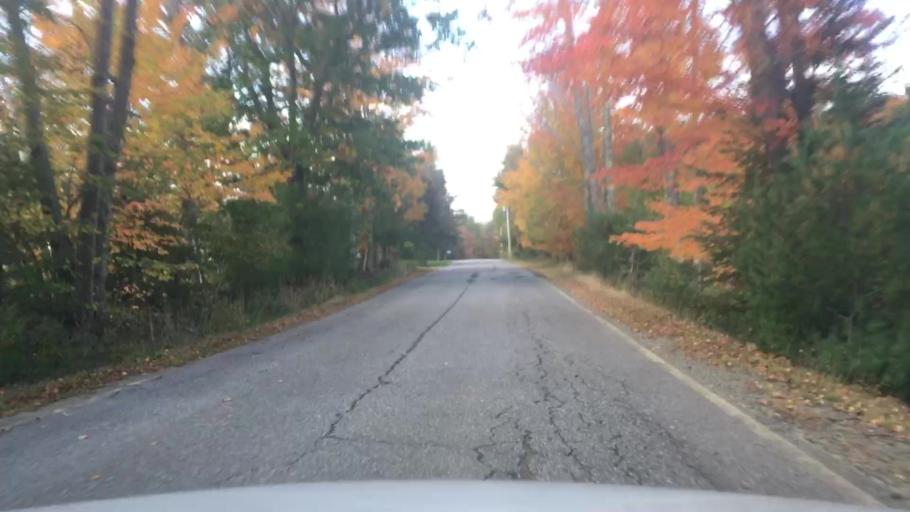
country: US
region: Maine
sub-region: Knox County
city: Washington
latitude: 44.3525
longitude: -69.3882
